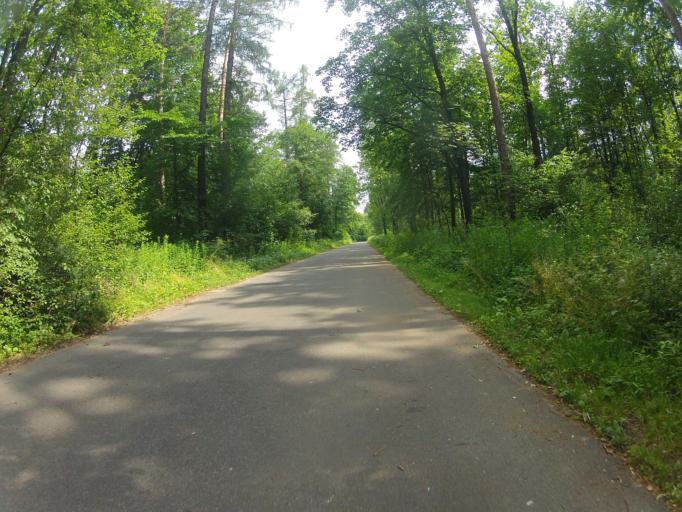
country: PL
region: Lesser Poland Voivodeship
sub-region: Powiat nowosadecki
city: Stary Sacz
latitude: 49.5659
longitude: 20.6583
